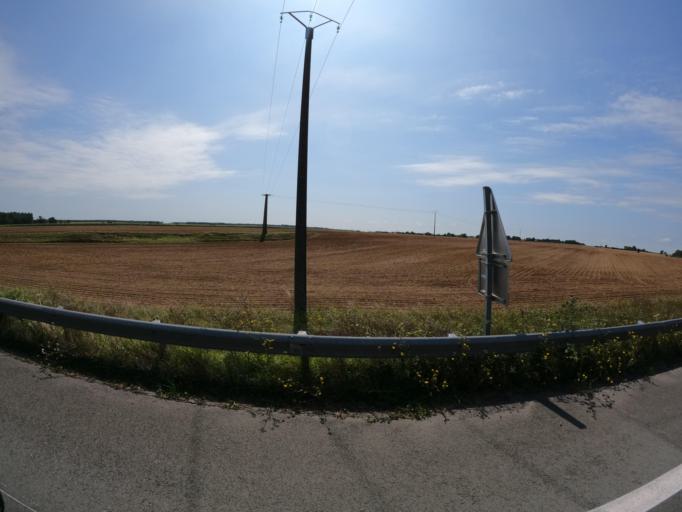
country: FR
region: Poitou-Charentes
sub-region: Departement des Deux-Sevres
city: Mauze-sur-le-Mignon
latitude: 46.2041
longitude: -0.6456
